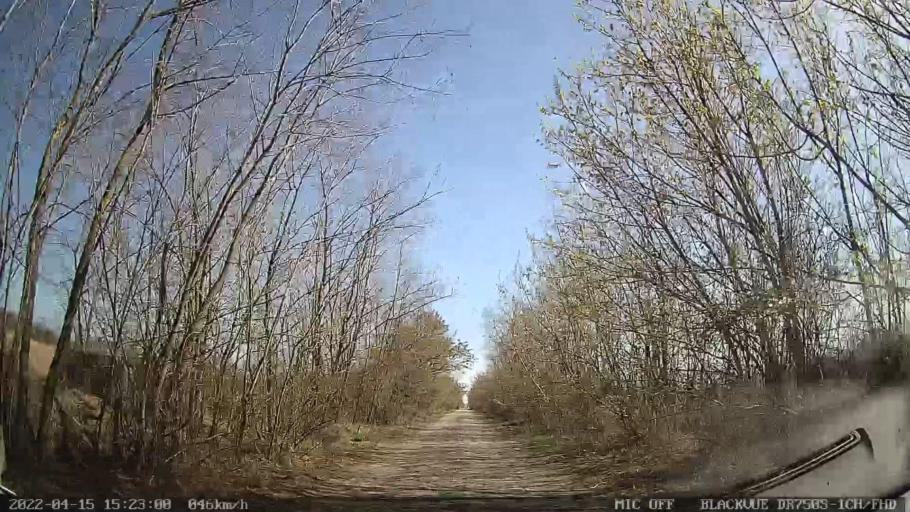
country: MD
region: Raionul Ocnita
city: Otaci
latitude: 48.3777
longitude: 27.9173
